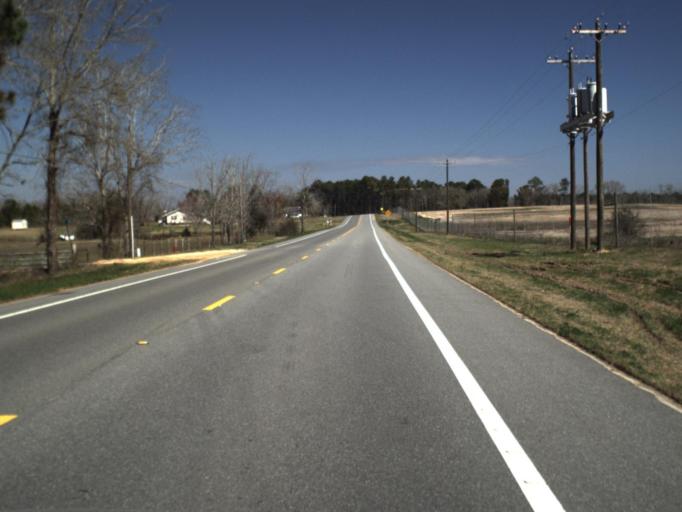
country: US
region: Florida
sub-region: Jackson County
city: Sneads
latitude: 30.6896
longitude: -85.0229
